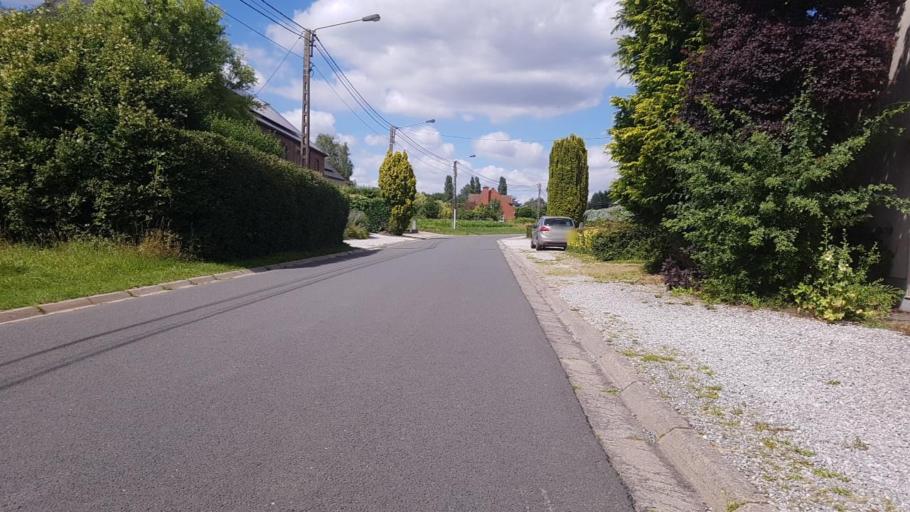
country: BE
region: Wallonia
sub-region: Province du Hainaut
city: Charleroi
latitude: 50.3374
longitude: 4.3923
